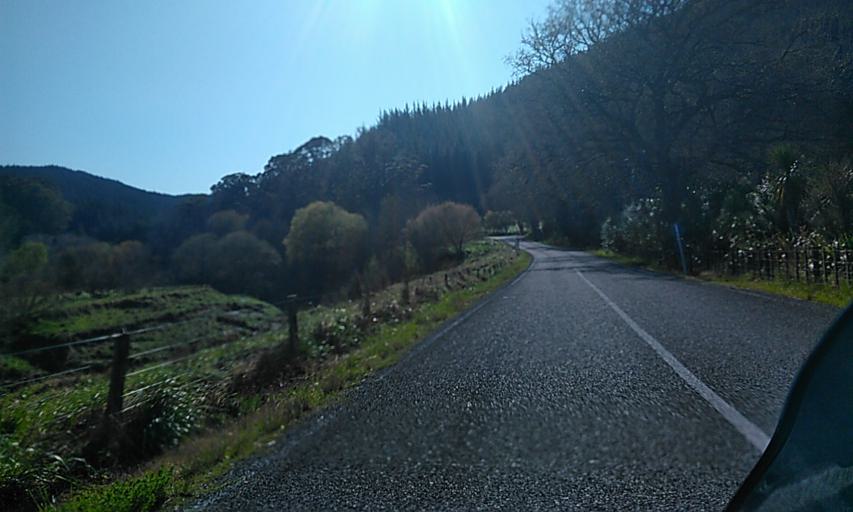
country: NZ
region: Gisborne
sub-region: Gisborne District
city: Gisborne
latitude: -38.5548
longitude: 178.0356
